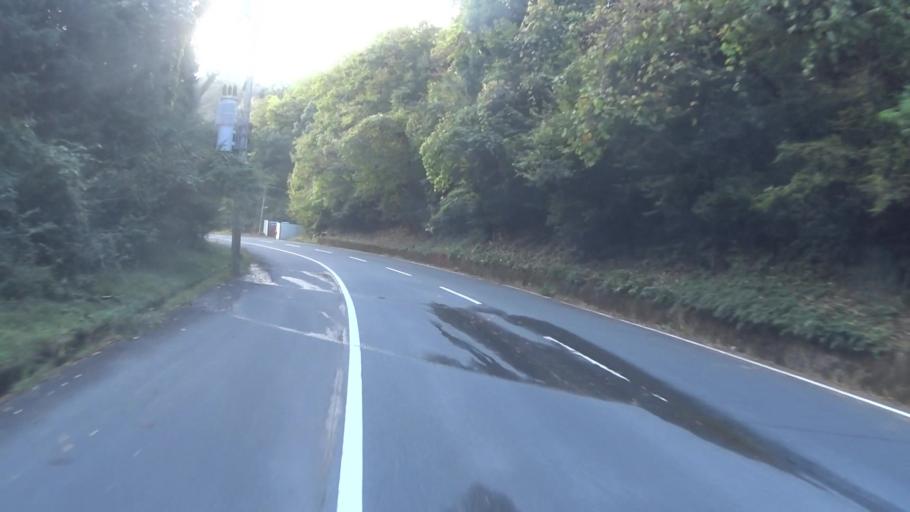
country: JP
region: Kyoto
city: Maizuru
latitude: 35.4647
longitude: 135.2455
